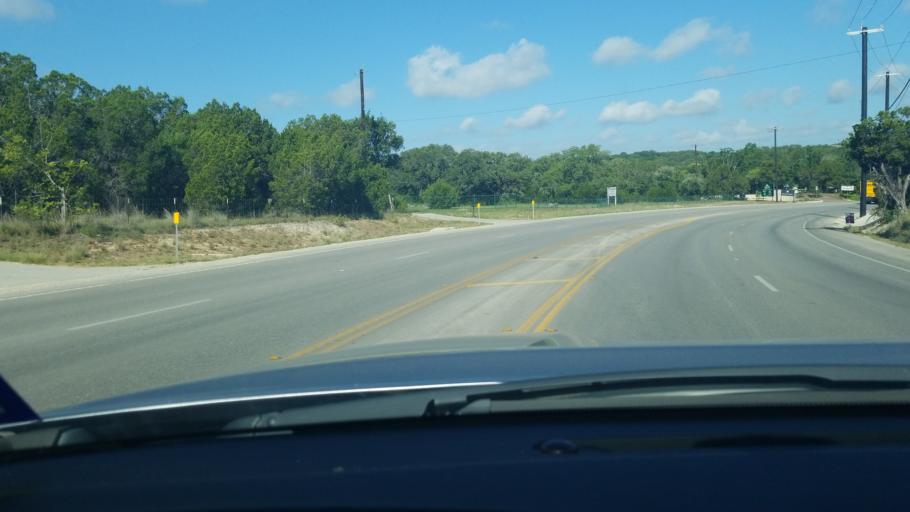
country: US
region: Texas
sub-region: Bexar County
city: Timberwood Park
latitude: 29.7126
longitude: -98.4654
